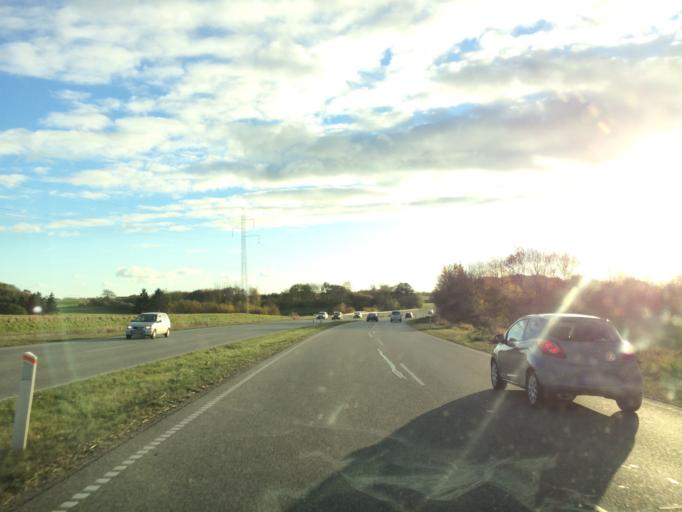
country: DK
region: South Denmark
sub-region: Sonderborg Kommune
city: Augustenborg
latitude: 54.9496
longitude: 9.8976
